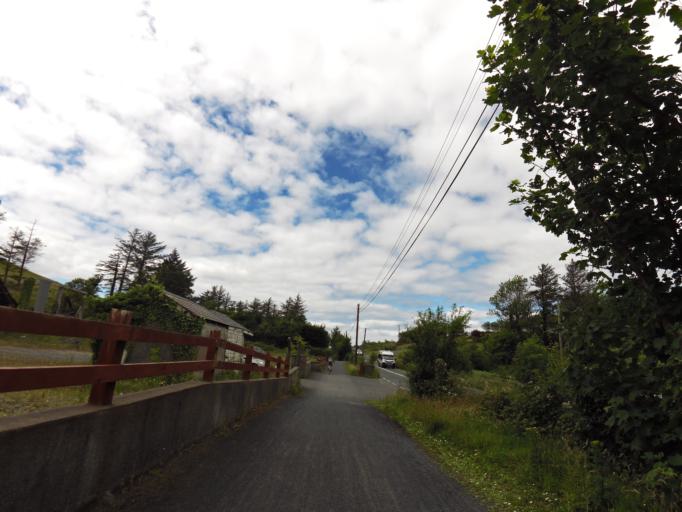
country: IE
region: Connaught
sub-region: Maigh Eo
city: Westport
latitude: 53.8226
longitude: -9.5375
